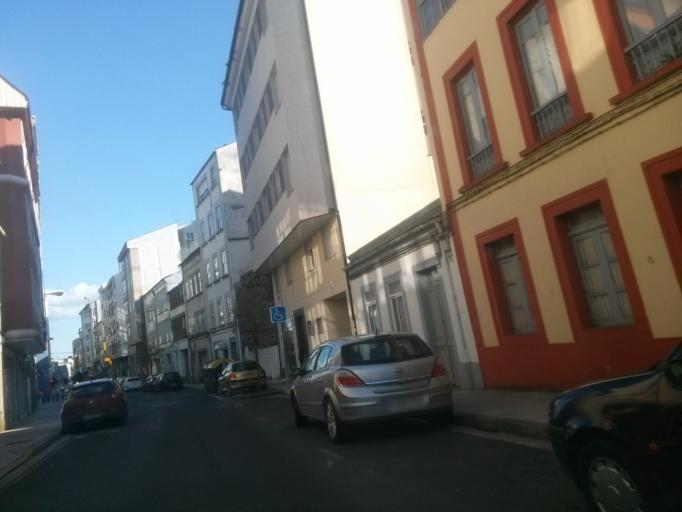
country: ES
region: Galicia
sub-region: Provincia de Lugo
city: Lugo
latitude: 43.0202
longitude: -7.5677
